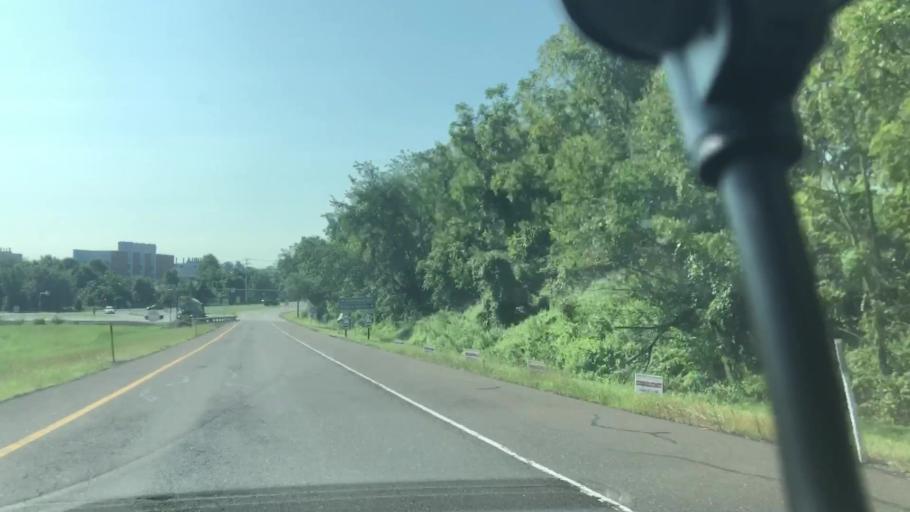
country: US
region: Pennsylvania
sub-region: Montgomery County
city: Trappe
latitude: 40.1614
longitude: -75.4833
